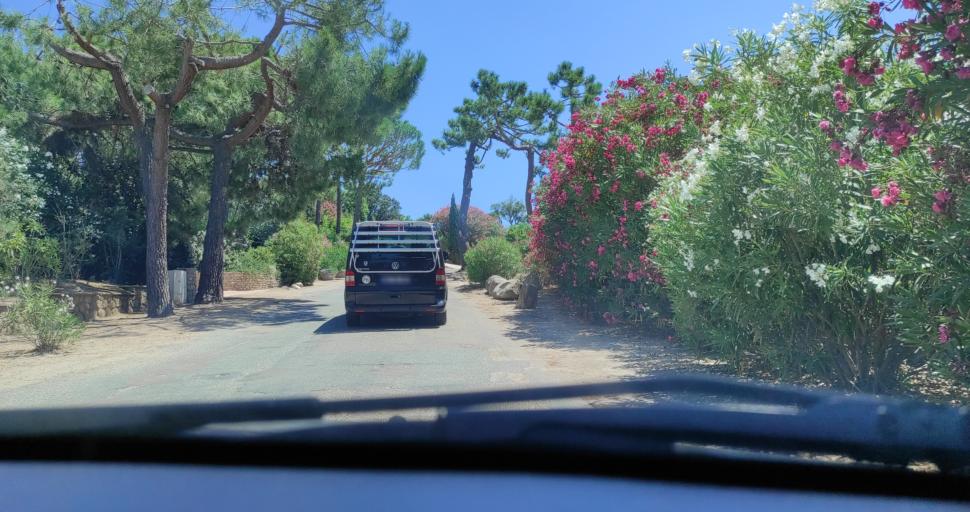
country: FR
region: Corsica
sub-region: Departement de la Corse-du-Sud
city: Porto-Vecchio
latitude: 41.6214
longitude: 9.3397
